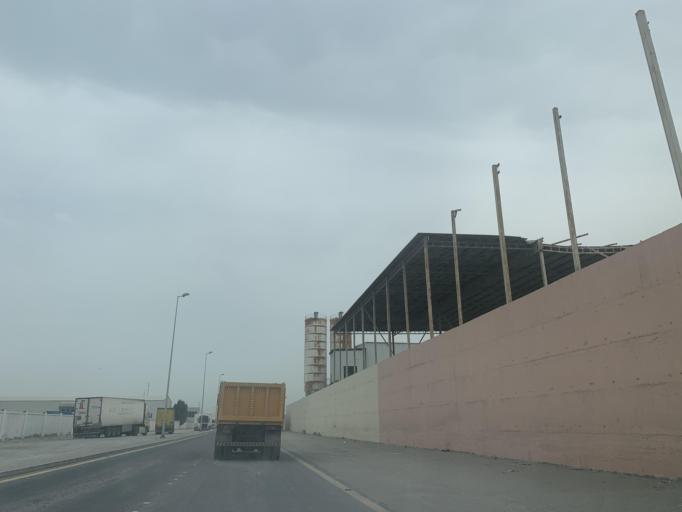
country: BH
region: Muharraq
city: Al Hadd
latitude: 26.2070
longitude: 50.6625
